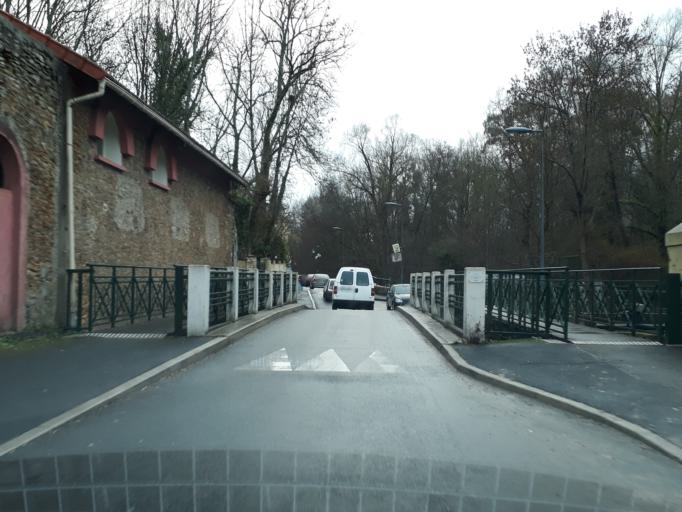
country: FR
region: Ile-de-France
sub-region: Departement de l'Essonne
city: Ormoy
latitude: 48.5795
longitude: 2.4445
